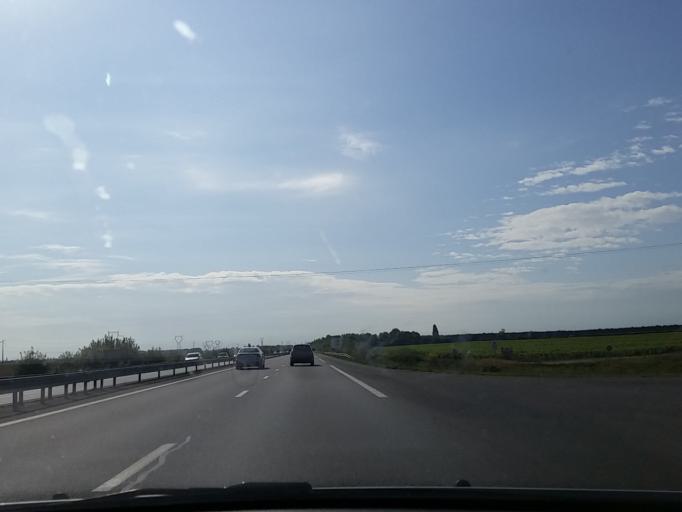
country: FR
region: Centre
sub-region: Departement du Cher
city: Marmagne
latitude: 47.0806
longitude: 2.2685
